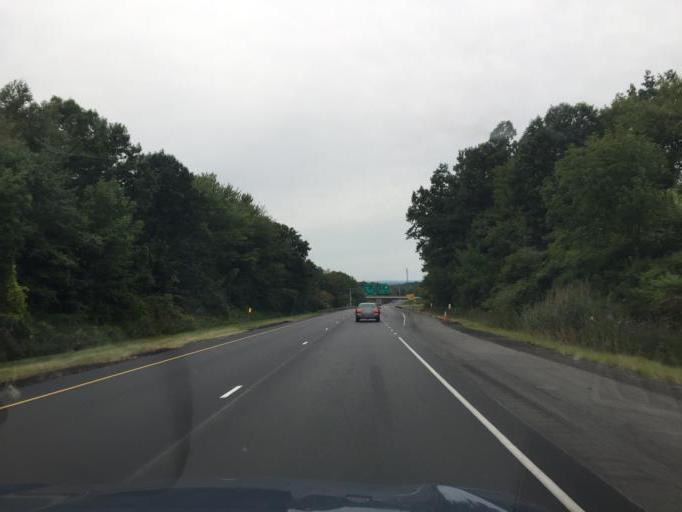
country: US
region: New York
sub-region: Columbia County
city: Niverville
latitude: 42.4829
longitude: -73.6626
